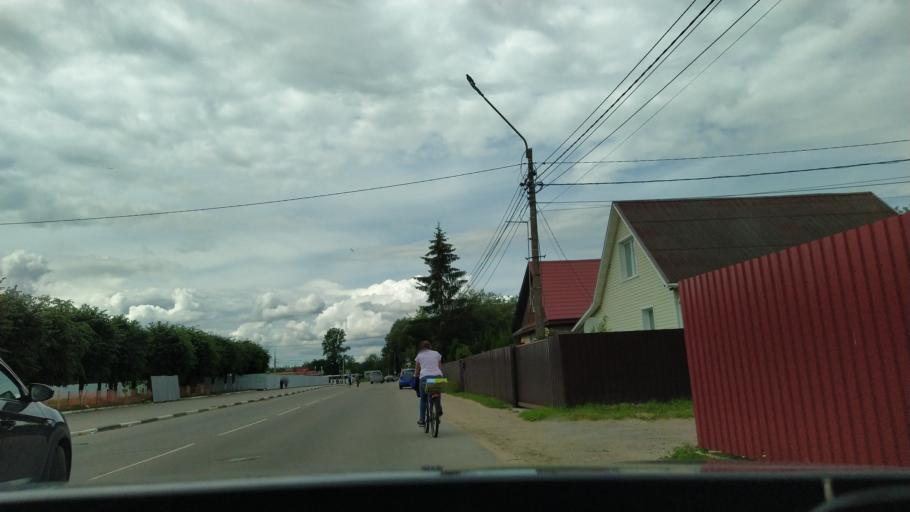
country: RU
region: Leningrad
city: Kirovsk
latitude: 59.8817
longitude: 30.9872
